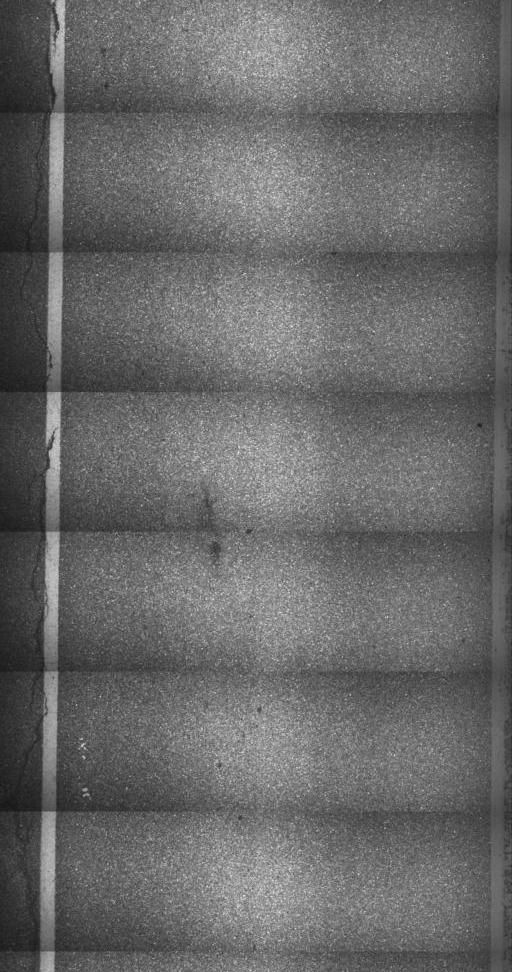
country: US
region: Vermont
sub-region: Orange County
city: Randolph
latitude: 43.8866
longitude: -72.8125
